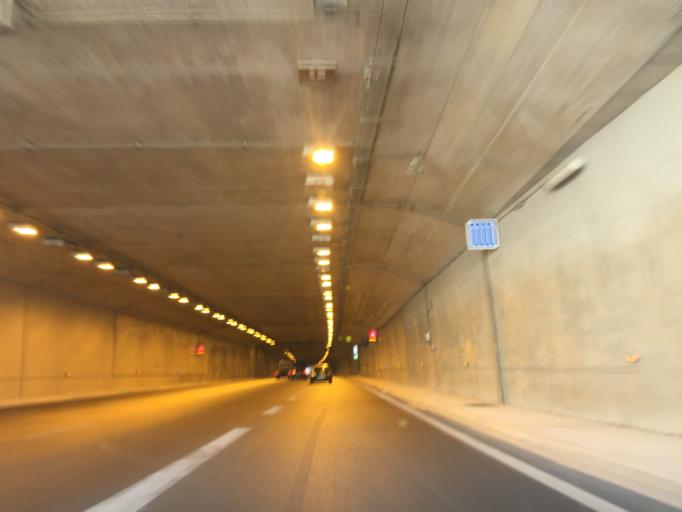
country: FR
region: Provence-Alpes-Cote d'Azur
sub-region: Departement des Bouches-du-Rhone
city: Marseille 12
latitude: 43.2935
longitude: 5.4242
